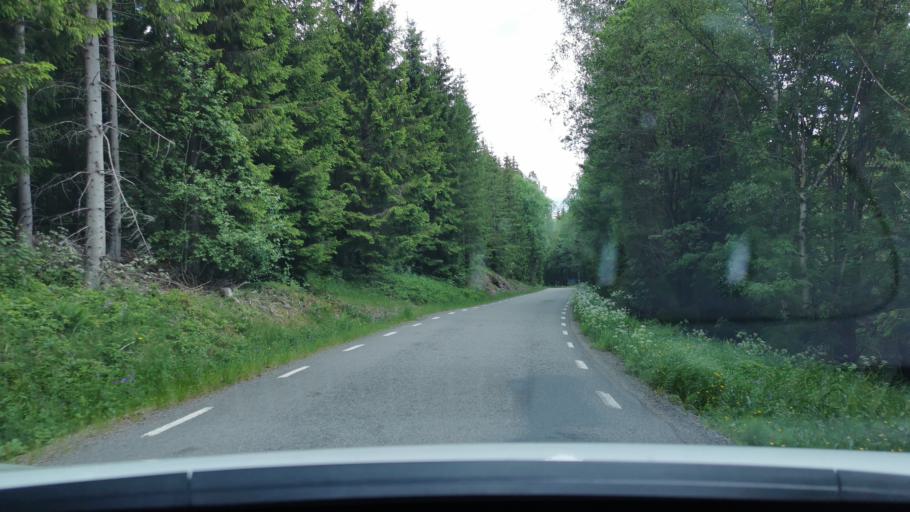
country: SE
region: Vaestra Goetaland
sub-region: Bengtsfors Kommun
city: Dals Langed
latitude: 58.8137
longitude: 12.3258
